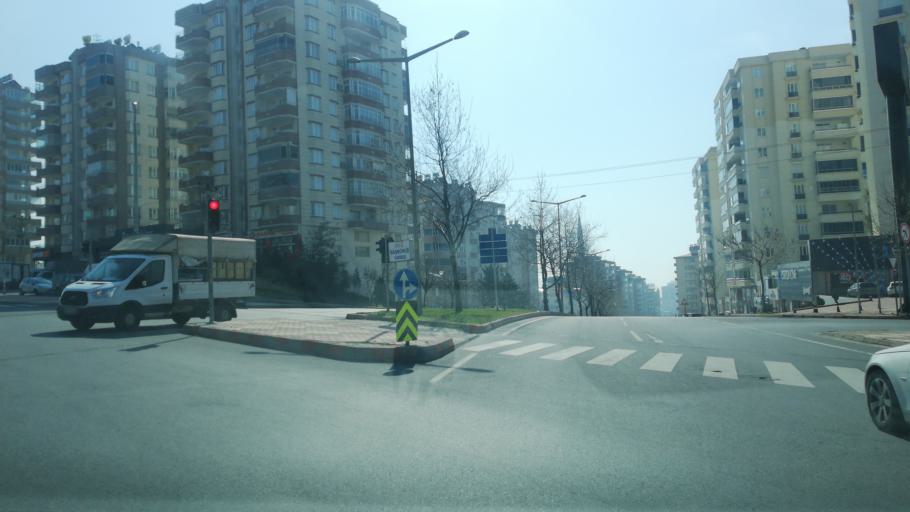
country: TR
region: Kahramanmaras
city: Kahramanmaras
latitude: 37.5890
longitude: 36.8778
